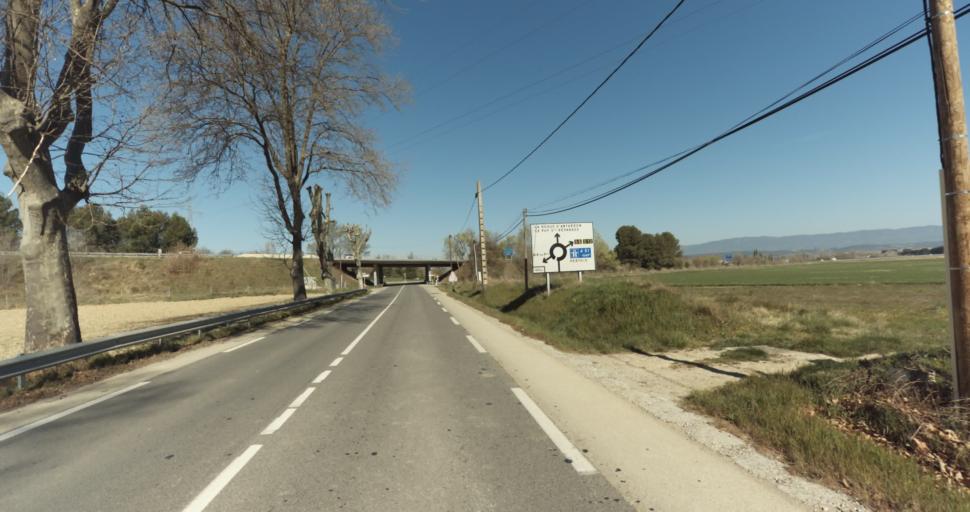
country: FR
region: Provence-Alpes-Cote d'Azur
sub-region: Departement des Bouches-du-Rhone
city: Meyrargues
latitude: 43.6464
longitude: 5.4934
